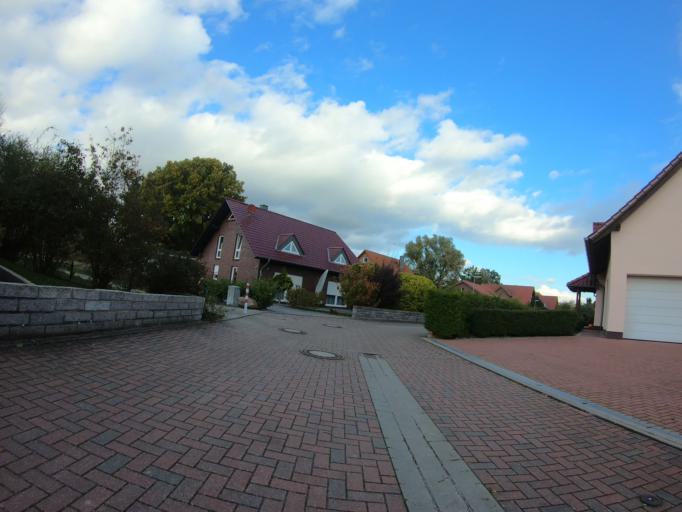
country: DE
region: Lower Saxony
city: Gifhorn
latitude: 52.5045
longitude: 10.5364
